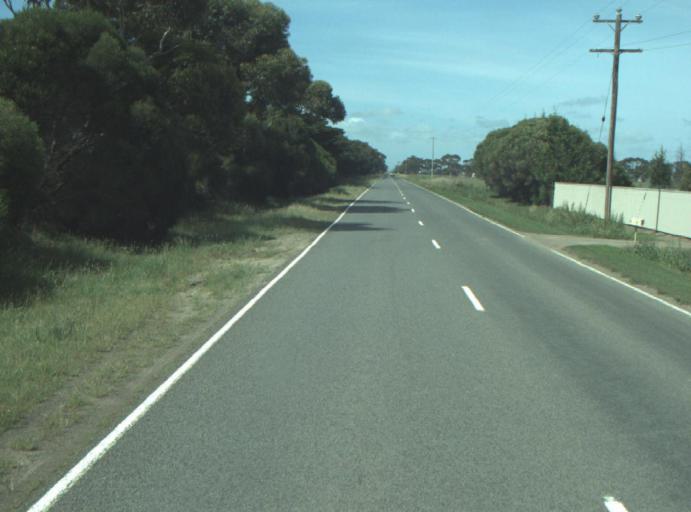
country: AU
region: Victoria
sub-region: Greater Geelong
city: Lara
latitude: -38.0477
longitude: 144.4291
